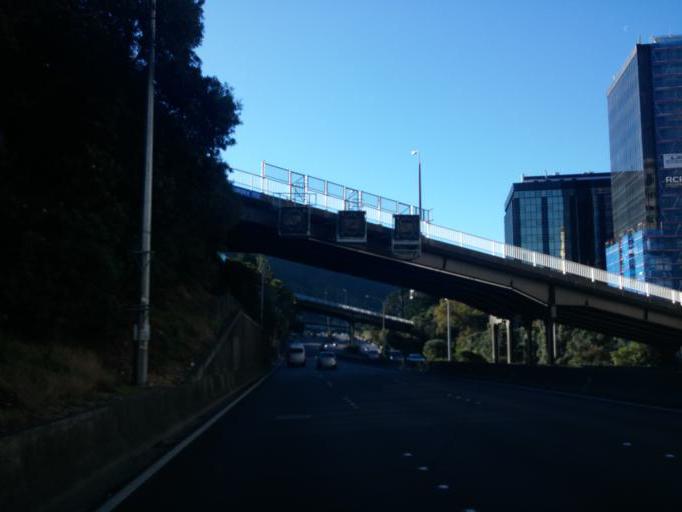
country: NZ
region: Wellington
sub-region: Wellington City
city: Wellington
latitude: -41.2818
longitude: 174.7737
